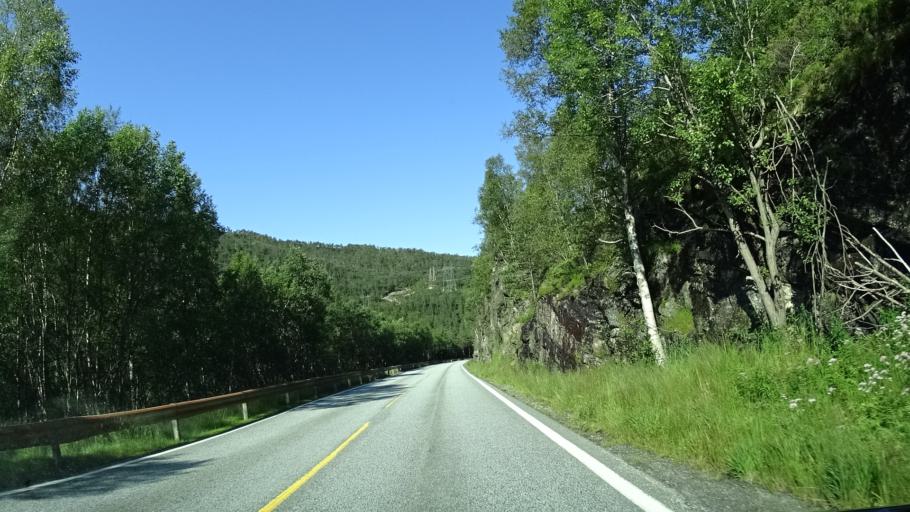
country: NO
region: Hordaland
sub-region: Samnanger
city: Tysse
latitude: 60.3811
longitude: 5.8682
